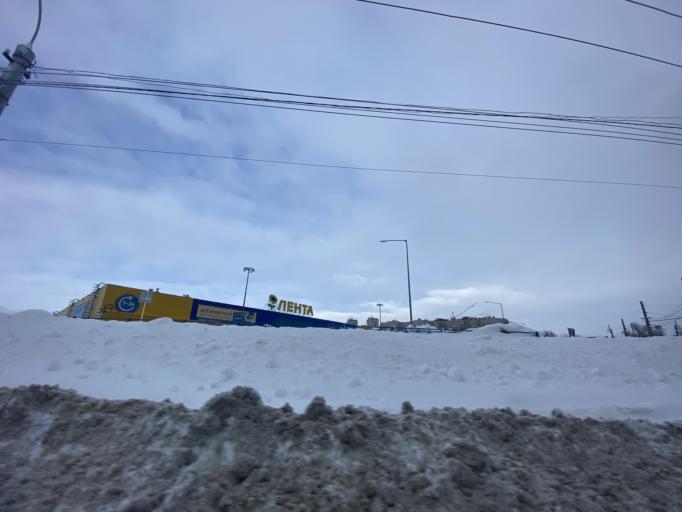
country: RU
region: Saratov
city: Engel's
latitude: 51.4962
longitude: 46.0926
